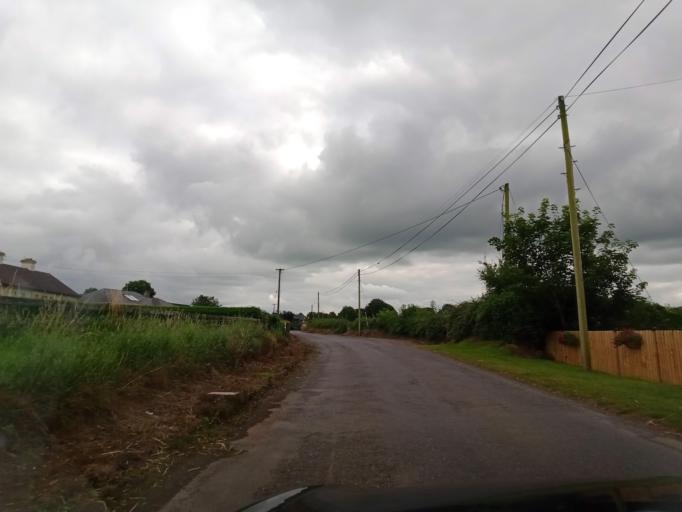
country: IE
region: Leinster
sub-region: Laois
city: Stradbally
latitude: 52.9789
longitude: -7.1625
